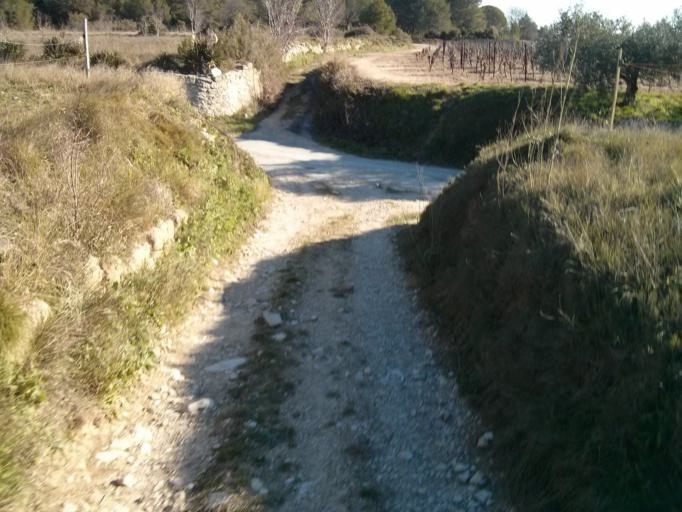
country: FR
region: Languedoc-Roussillon
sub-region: Departement du Gard
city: Aigues-Vives
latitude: 43.7535
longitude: 4.1862
